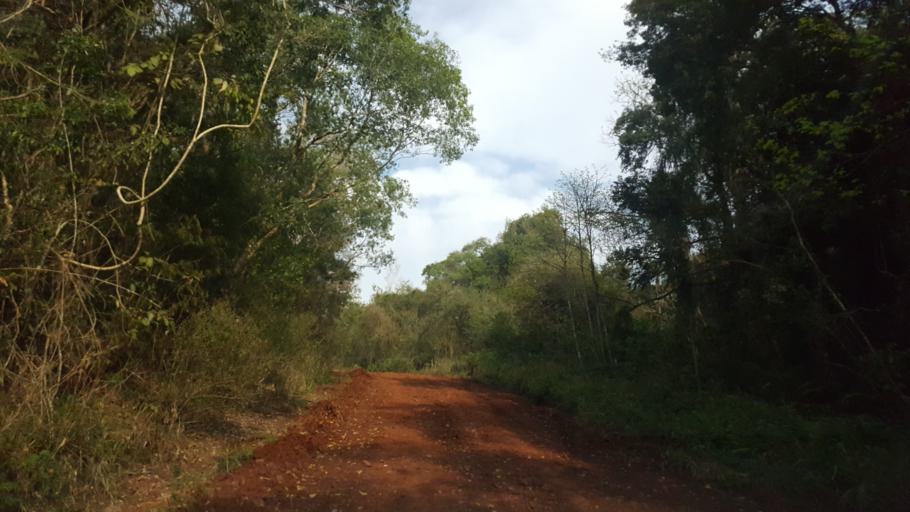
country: AR
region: Misiones
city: Capiovi
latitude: -26.9039
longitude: -55.1143
